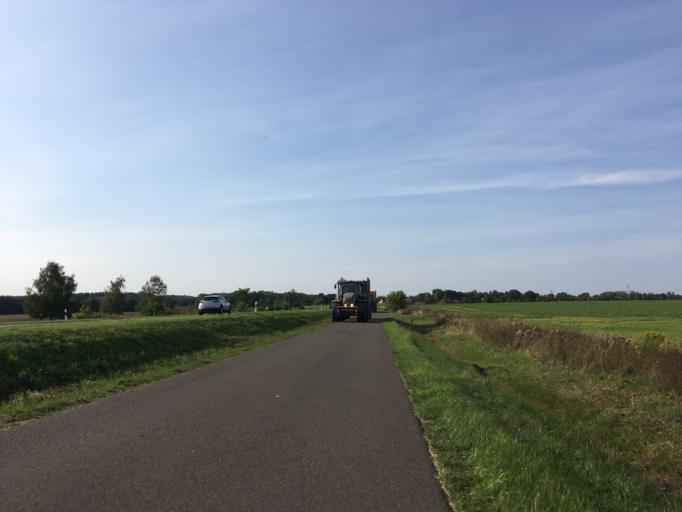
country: DE
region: Brandenburg
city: Brieskow-Finkenheerd
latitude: 52.2776
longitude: 14.5594
